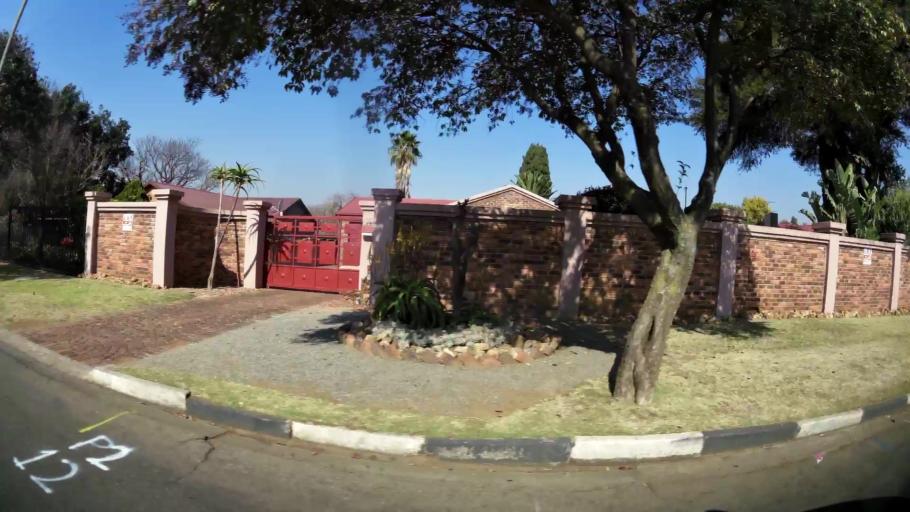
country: ZA
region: Gauteng
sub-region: Ekurhuleni Metropolitan Municipality
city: Boksburg
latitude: -26.1628
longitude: 28.2710
